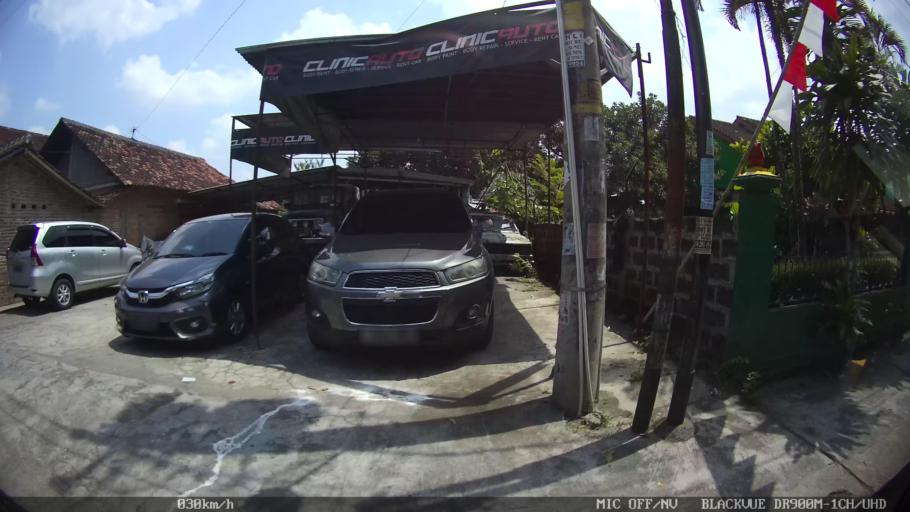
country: ID
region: Daerah Istimewa Yogyakarta
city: Yogyakarta
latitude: -7.8193
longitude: 110.4075
